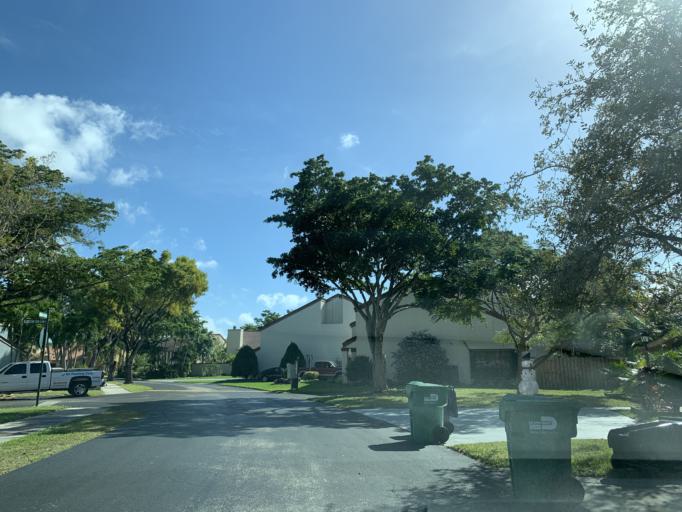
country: US
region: Florida
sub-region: Miami-Dade County
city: The Hammocks
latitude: 25.6840
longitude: -80.4386
